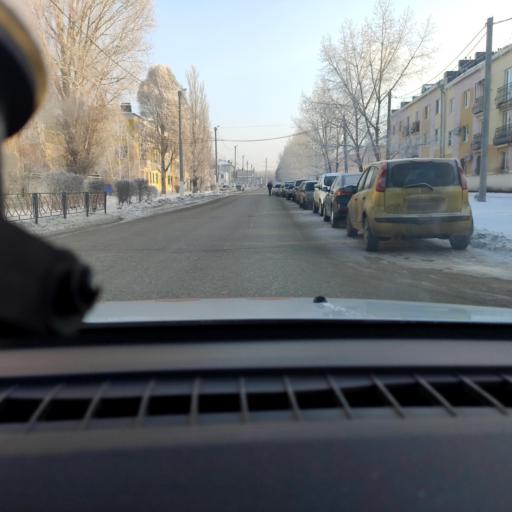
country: RU
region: Samara
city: Chapayevsk
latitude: 52.9732
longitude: 49.7019
